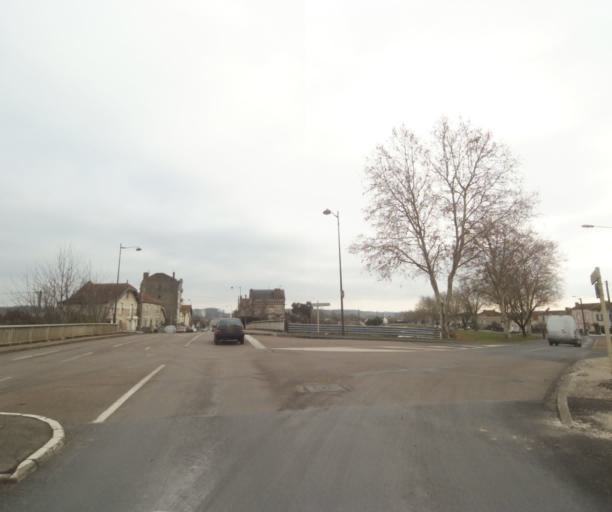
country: FR
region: Champagne-Ardenne
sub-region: Departement de la Haute-Marne
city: Bettancourt-la-Ferree
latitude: 48.6358
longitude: 4.9643
